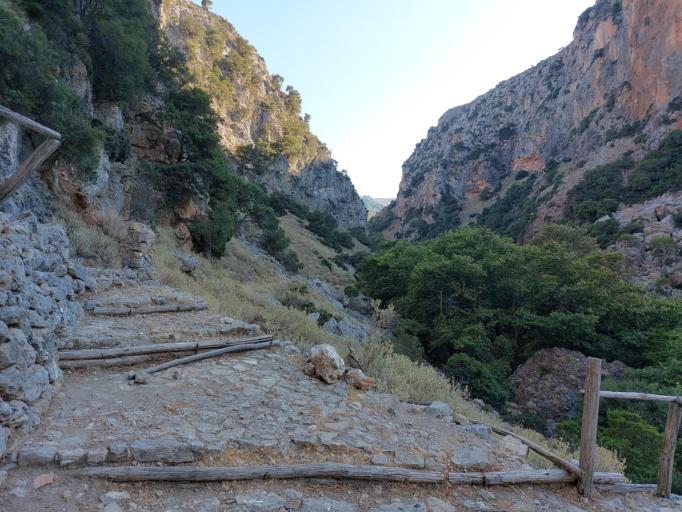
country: GR
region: Crete
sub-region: Nomos Chanias
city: Vryses
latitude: 35.4361
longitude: 23.6502
